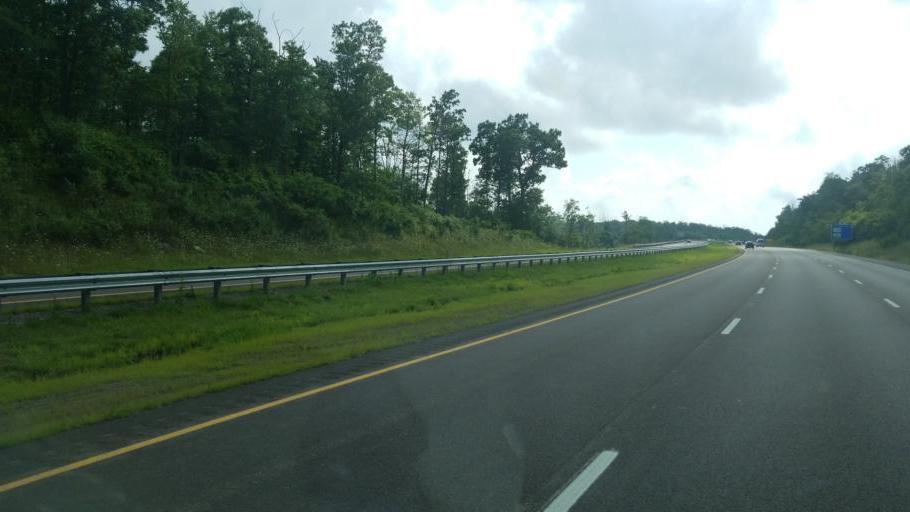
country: US
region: Pennsylvania
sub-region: Somerset County
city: Meyersdale
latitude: 39.6839
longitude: -79.2078
